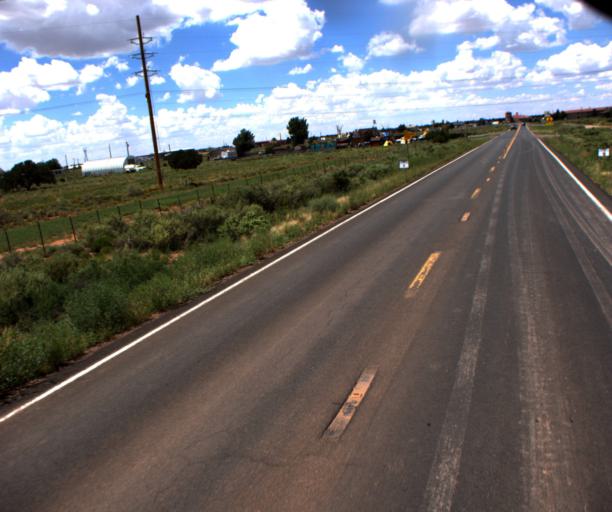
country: US
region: Arizona
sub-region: Coconino County
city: Grand Canyon Village
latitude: 35.6486
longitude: -112.1345
